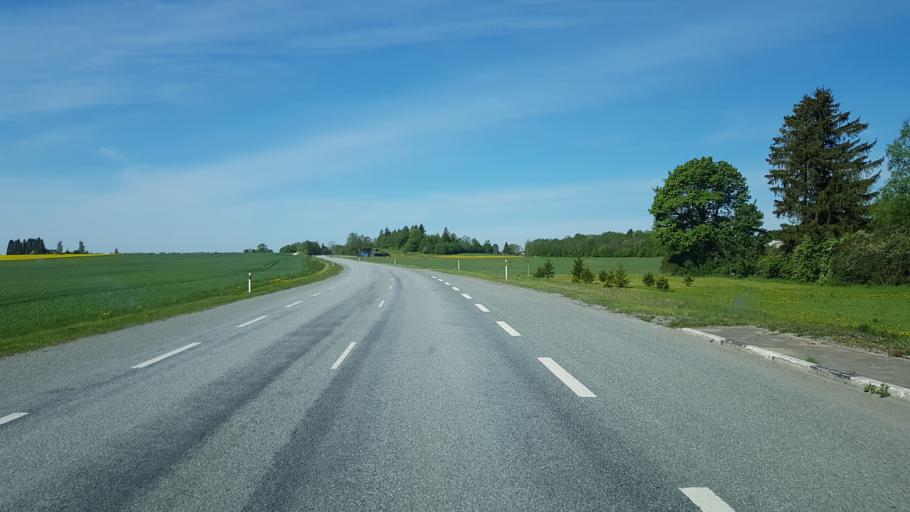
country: EE
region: Jogevamaa
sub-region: Poltsamaa linn
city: Poltsamaa
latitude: 58.6780
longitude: 26.0246
